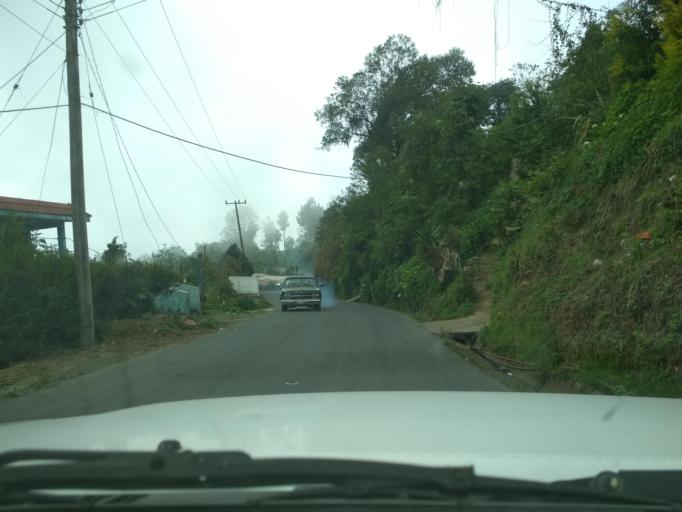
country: MX
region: Veracruz
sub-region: La Perla
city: Chilapa
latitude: 18.9648
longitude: -97.1680
